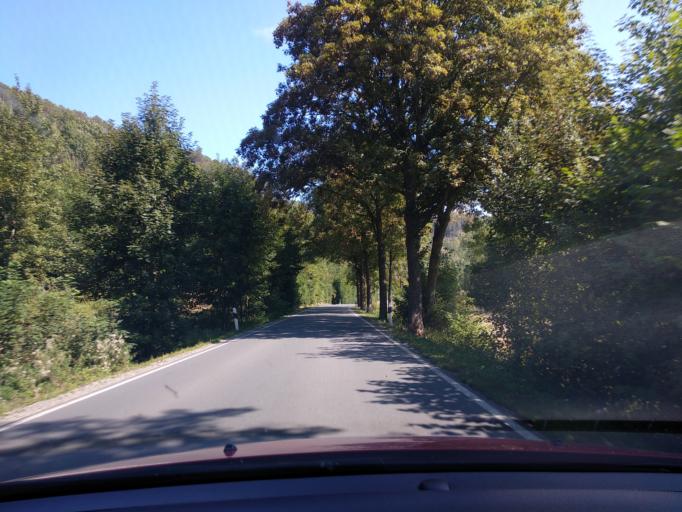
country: DE
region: North Rhine-Westphalia
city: Beverungen
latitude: 51.6802
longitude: 9.3451
